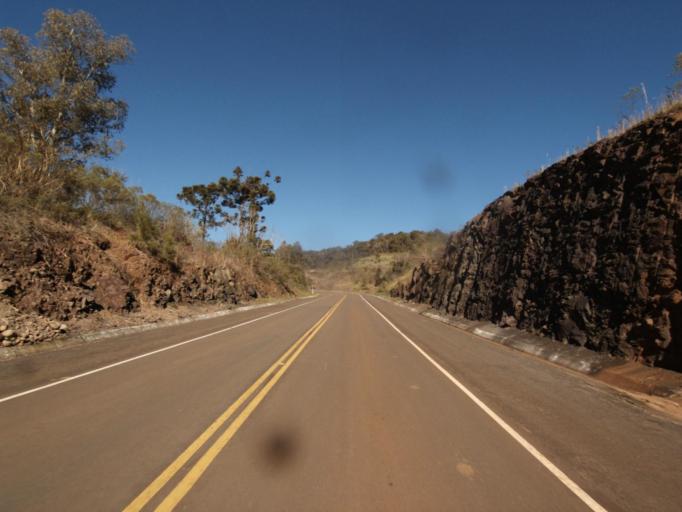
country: AR
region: Misiones
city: Bernardo de Irigoyen
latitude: -26.6104
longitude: -53.7263
